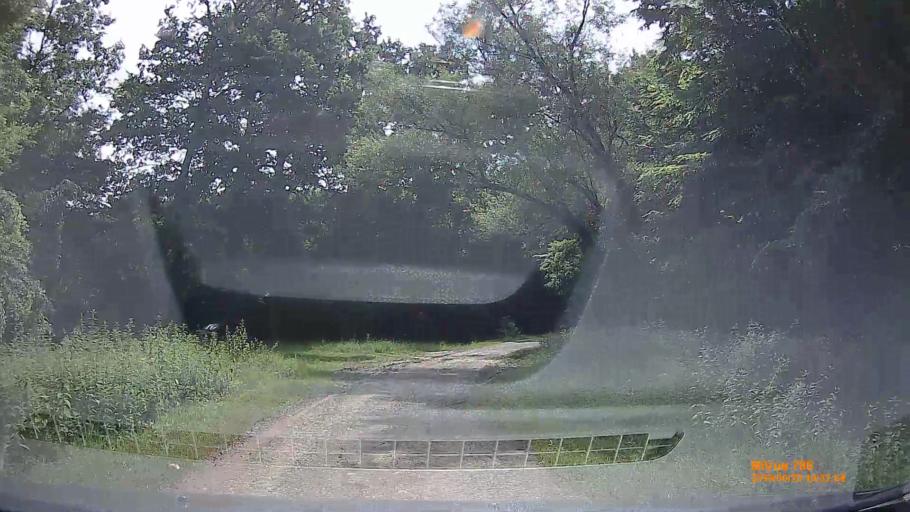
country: HU
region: Baranya
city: Mecseknadasd
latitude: 46.2081
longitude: 18.5140
